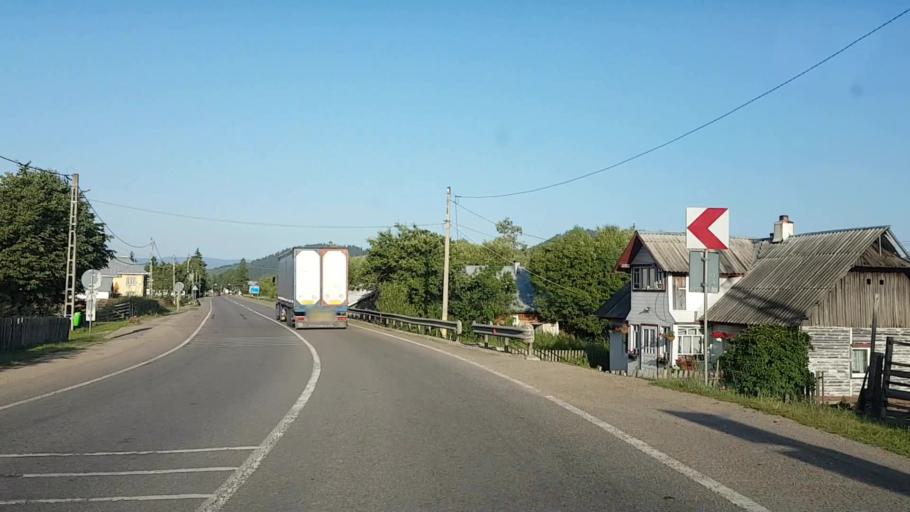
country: RO
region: Suceava
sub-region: Comuna Dorna Candrenilor
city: Dorna Candrenilor
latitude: 47.3568
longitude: 25.2362
